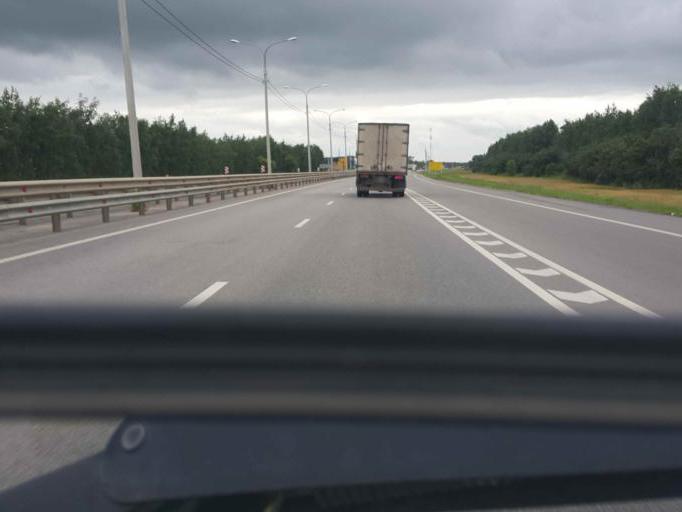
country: RU
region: Tambov
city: Zavoronezhskoye
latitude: 52.8556
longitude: 40.7789
